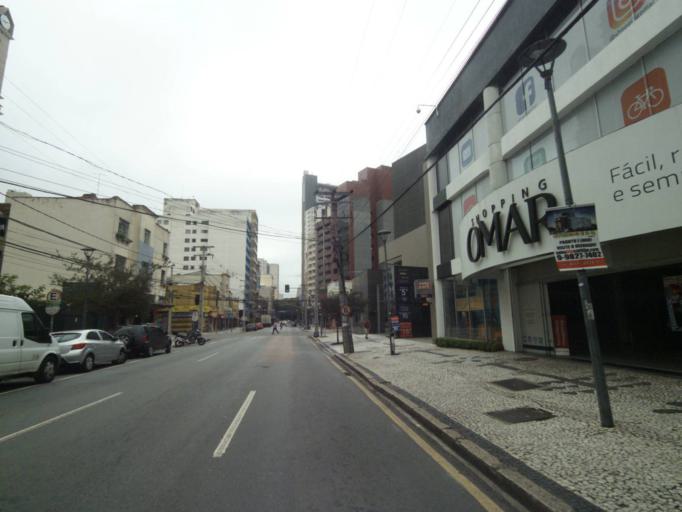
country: BR
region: Parana
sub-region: Curitiba
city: Curitiba
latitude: -25.4344
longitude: -49.2797
